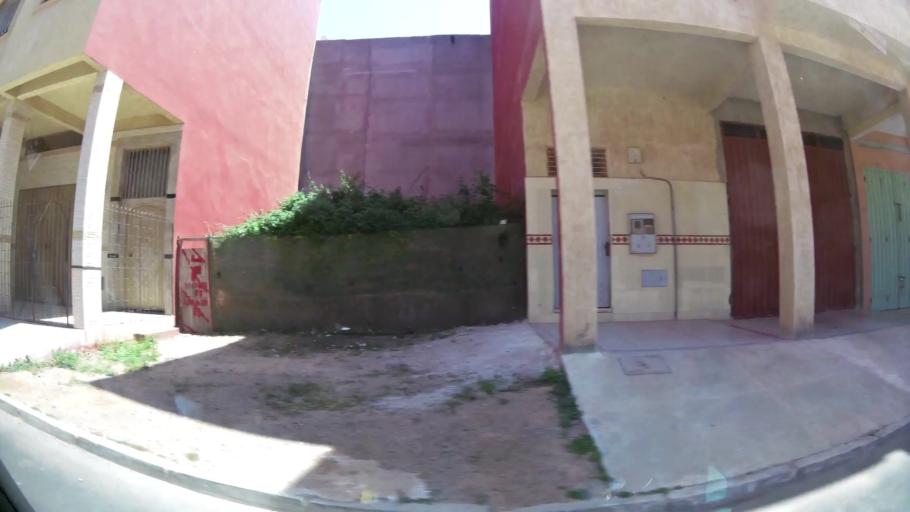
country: MA
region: Souss-Massa-Draa
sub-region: Inezgane-Ait Mellou
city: Inezgane
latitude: 30.3463
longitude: -9.4830
